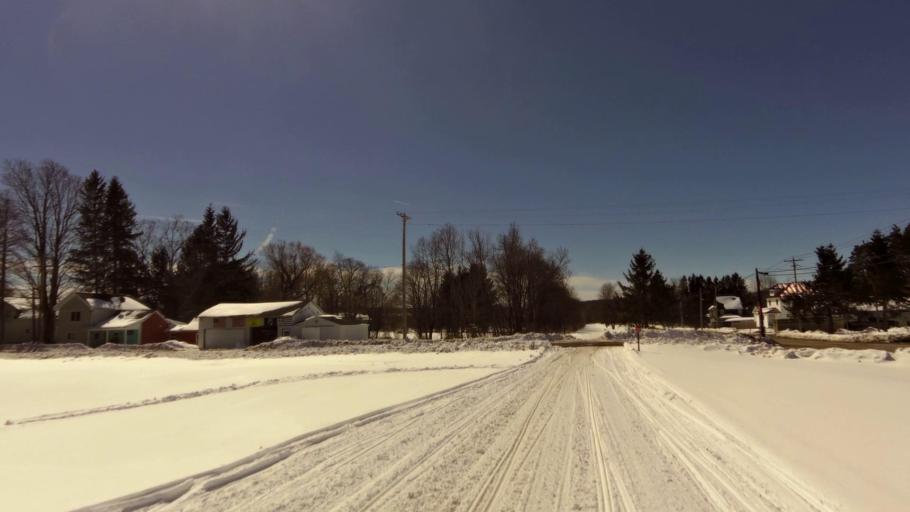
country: US
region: New York
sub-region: Wyoming County
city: Arcade
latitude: 42.4276
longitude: -78.3604
